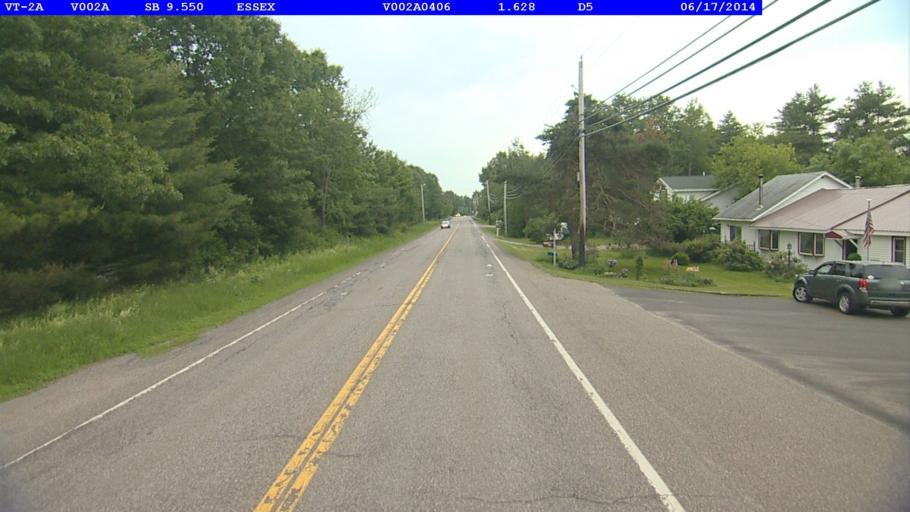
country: US
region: Vermont
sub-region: Chittenden County
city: Essex Junction
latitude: 44.5039
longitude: -73.1155
